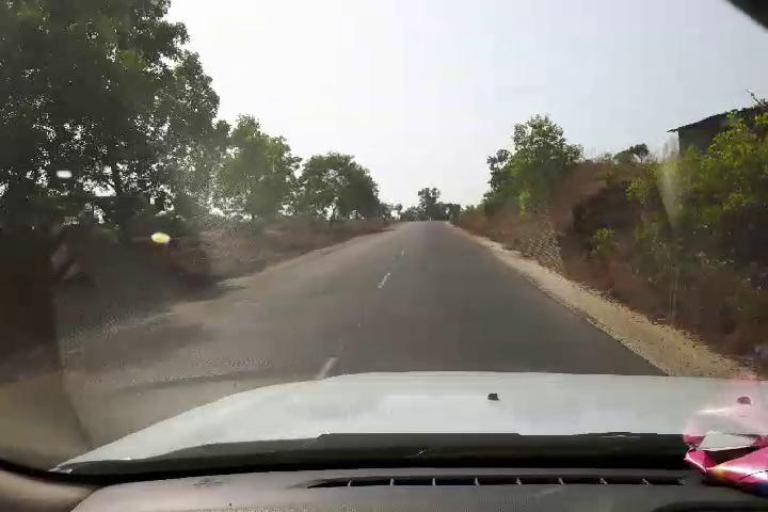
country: SL
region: Western Area
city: Hastings
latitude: 8.3147
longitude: -13.1890
